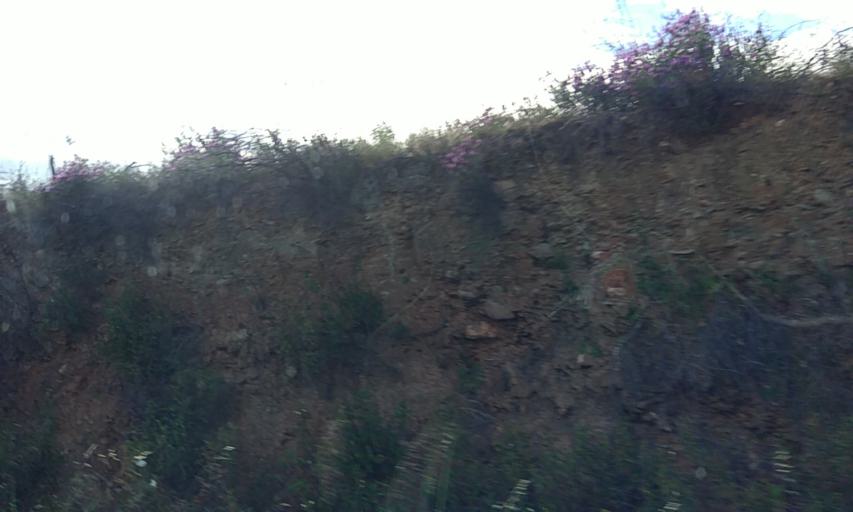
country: ES
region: Extremadura
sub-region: Provincia de Caceres
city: Moraleja
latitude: 40.1055
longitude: -6.6752
